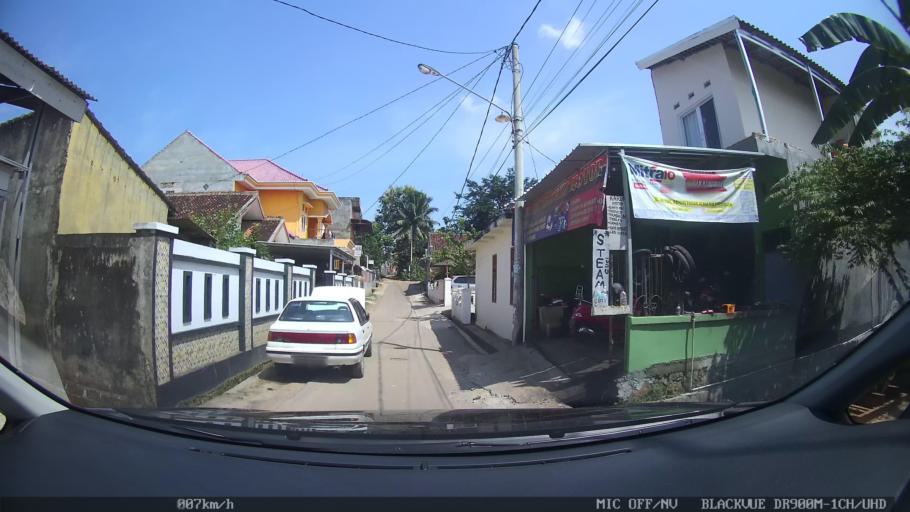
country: ID
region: Lampung
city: Kedaton
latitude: -5.3665
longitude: 105.2495
